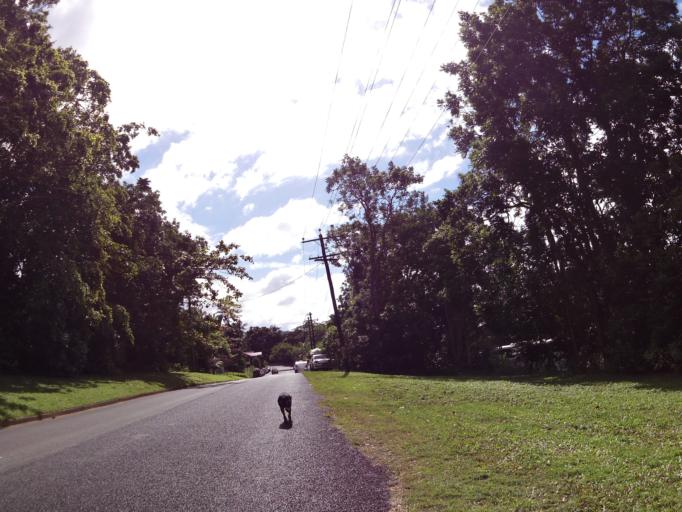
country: AU
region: Queensland
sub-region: Tablelands
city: Kuranda
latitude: -16.8199
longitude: 145.6389
